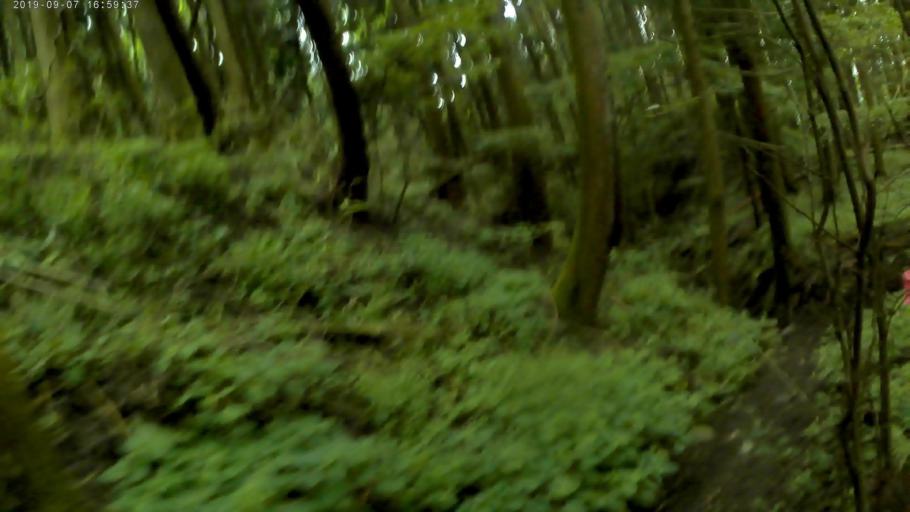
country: JP
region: Gunma
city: Annaka
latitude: 36.3579
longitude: 138.7065
